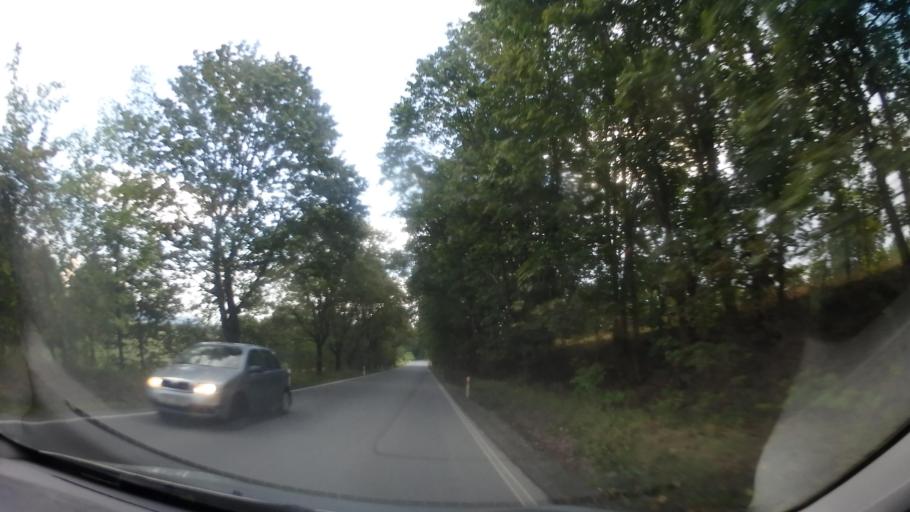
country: CZ
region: Olomoucky
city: Zabreh
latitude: 49.8874
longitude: 16.8426
